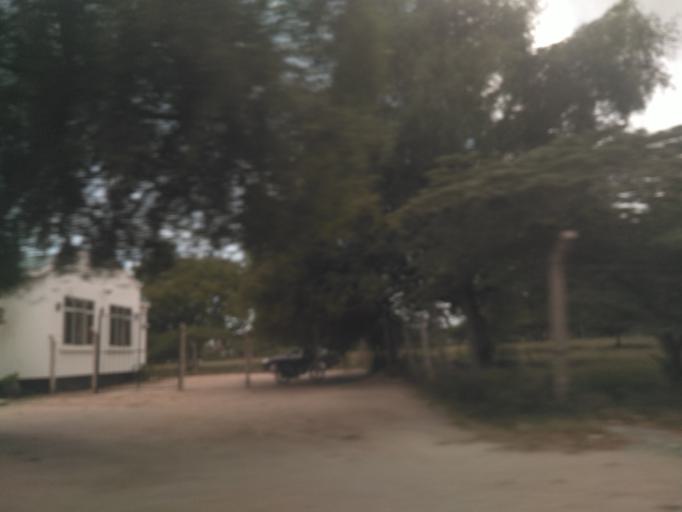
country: TZ
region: Dar es Salaam
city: Dar es Salaam
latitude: -6.8515
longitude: 39.2715
